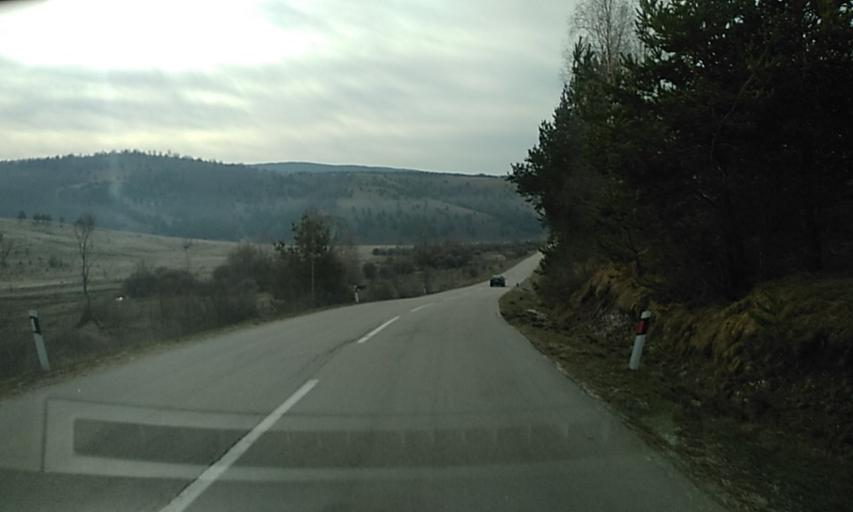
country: RS
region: Central Serbia
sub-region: Pcinjski Okrug
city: Bosilegrad
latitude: 42.6307
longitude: 22.3932
